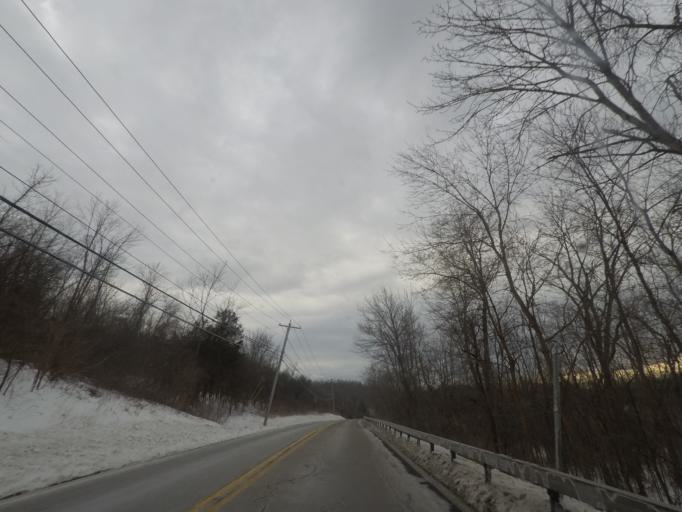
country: US
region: New York
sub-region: Rensselaer County
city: Castleton-on-Hudson
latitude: 42.5231
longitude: -73.7576
